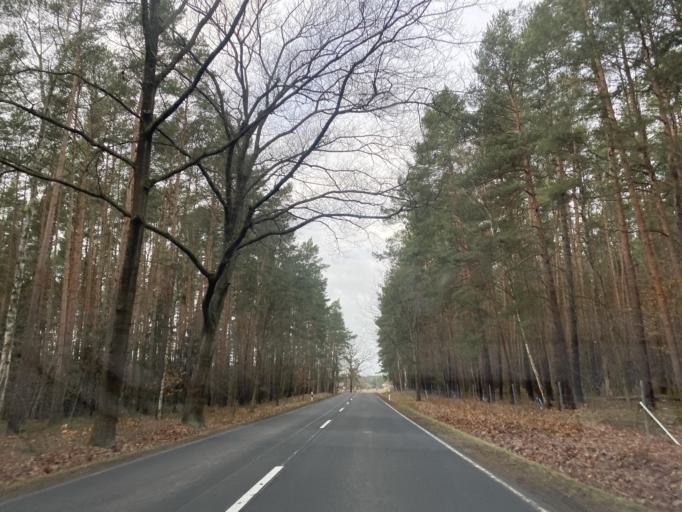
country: PL
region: Lubusz
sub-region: Powiat zarski
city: Leknica
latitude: 51.5090
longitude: 14.7830
